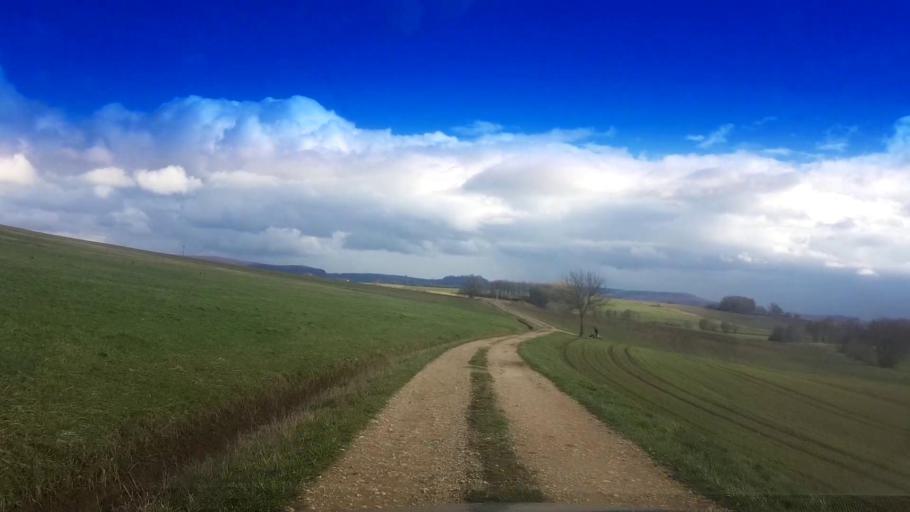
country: DE
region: Bavaria
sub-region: Upper Franconia
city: Schesslitz
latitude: 49.9958
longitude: 11.0144
